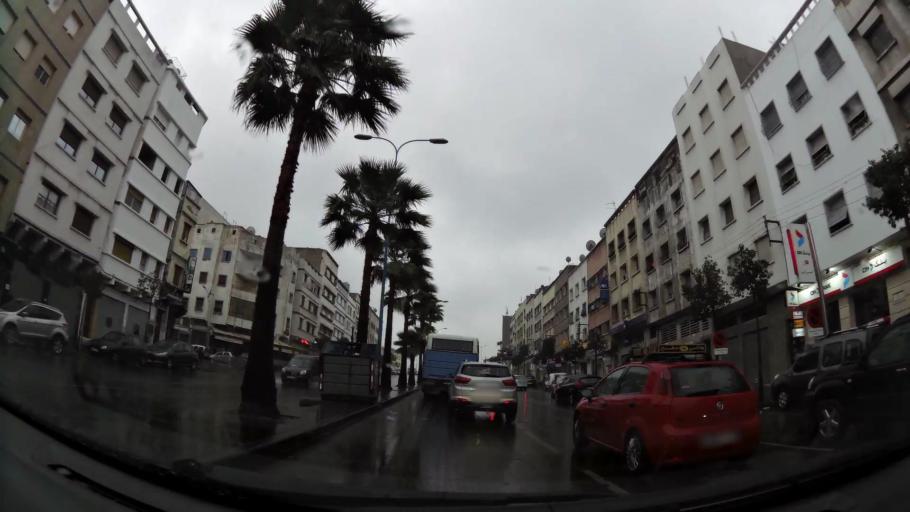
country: MA
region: Grand Casablanca
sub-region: Casablanca
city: Casablanca
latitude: 33.5636
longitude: -7.6094
